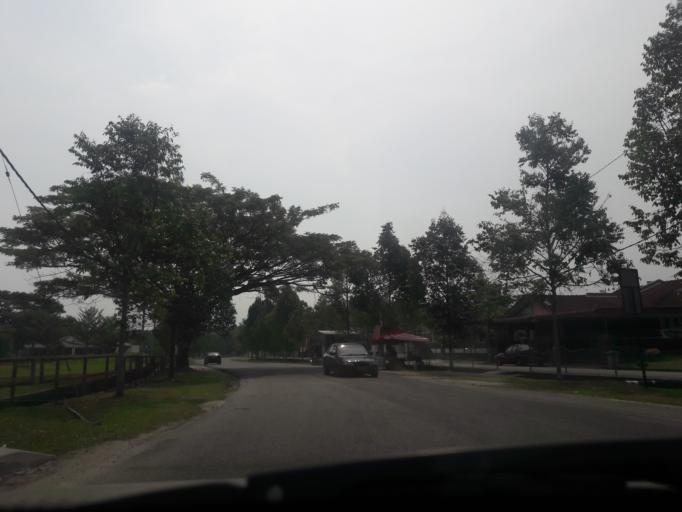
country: MY
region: Kedah
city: Kulim
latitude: 5.3683
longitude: 100.5609
